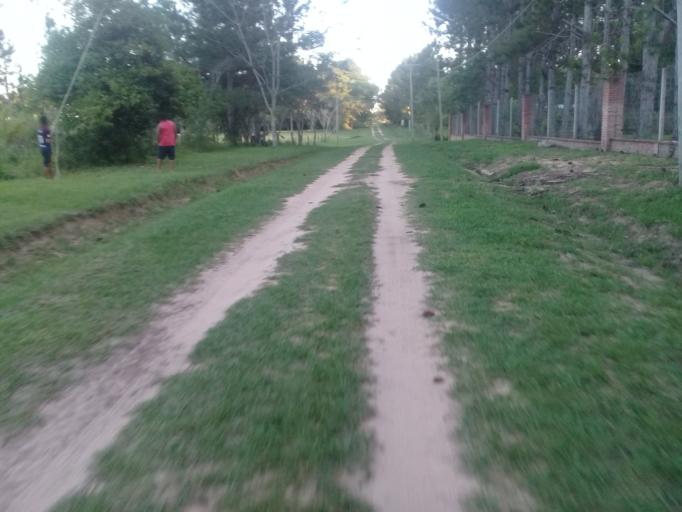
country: AR
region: Corrientes
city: San Luis del Palmar
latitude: -27.4694
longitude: -58.6662
